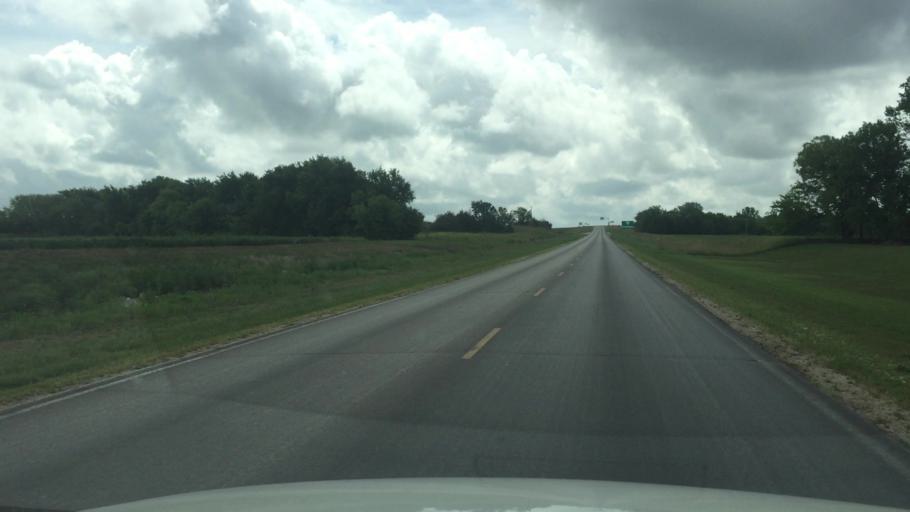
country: US
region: Kansas
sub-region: Allen County
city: Iola
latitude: 37.8863
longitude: -95.4040
